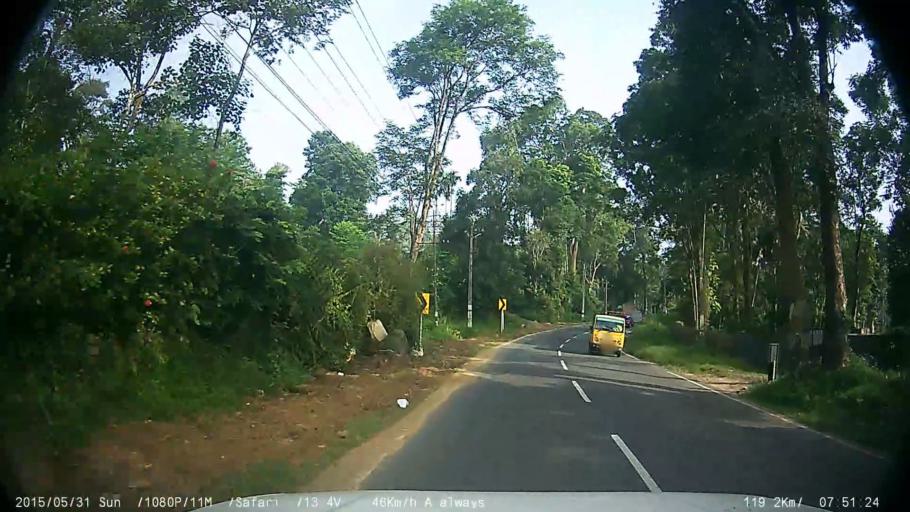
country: IN
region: Kerala
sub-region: Wayanad
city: Kalpetta
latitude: 11.6351
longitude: 76.0877
